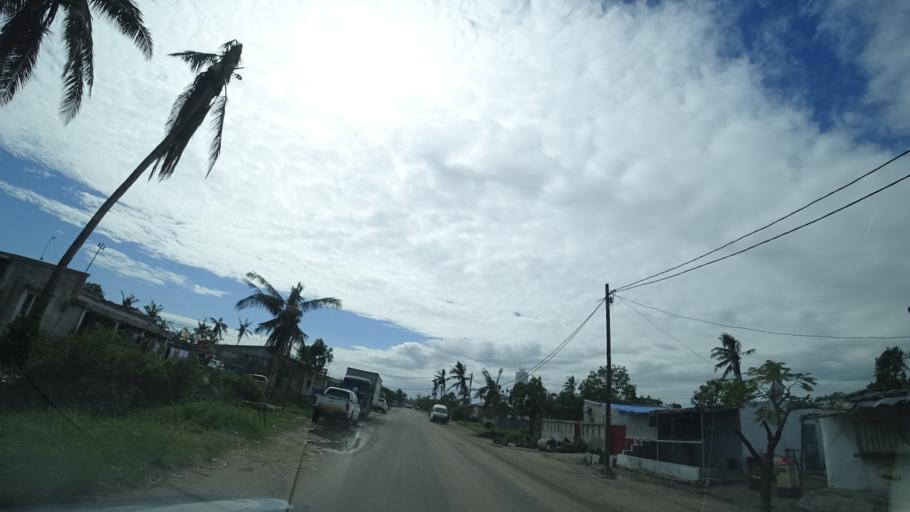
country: MZ
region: Sofala
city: Beira
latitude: -19.7609
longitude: 34.8653
